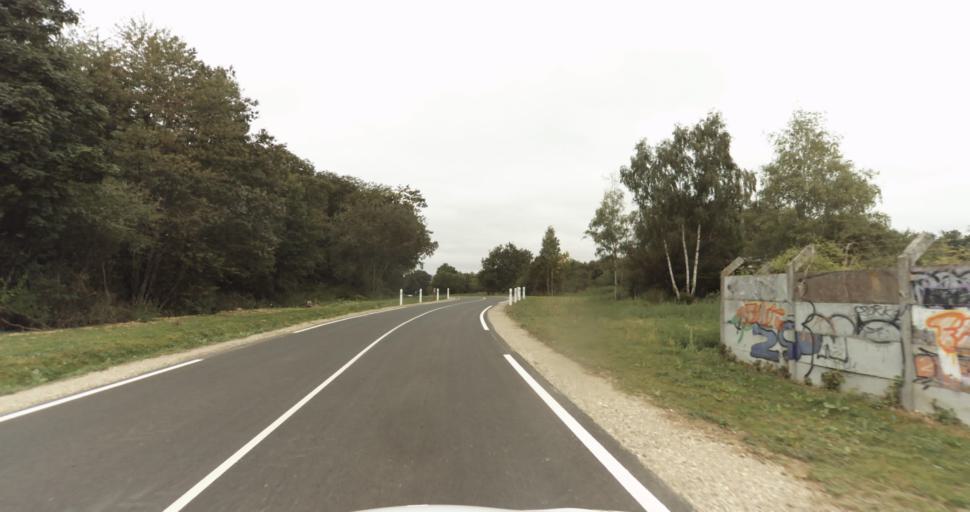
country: FR
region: Haute-Normandie
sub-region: Departement de l'Eure
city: Gravigny
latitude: 49.0343
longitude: 1.1799
